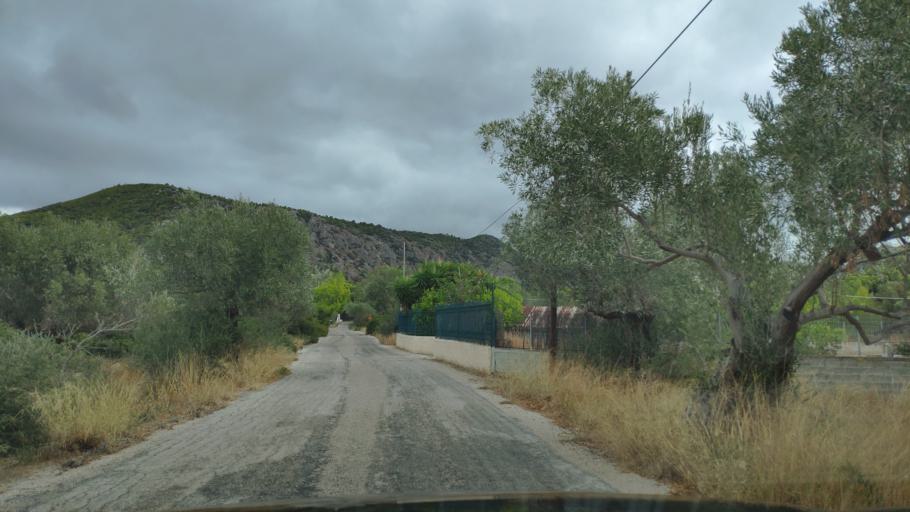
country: GR
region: Peloponnese
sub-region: Nomos Korinthias
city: Perachora
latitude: 38.0312
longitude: 22.8649
